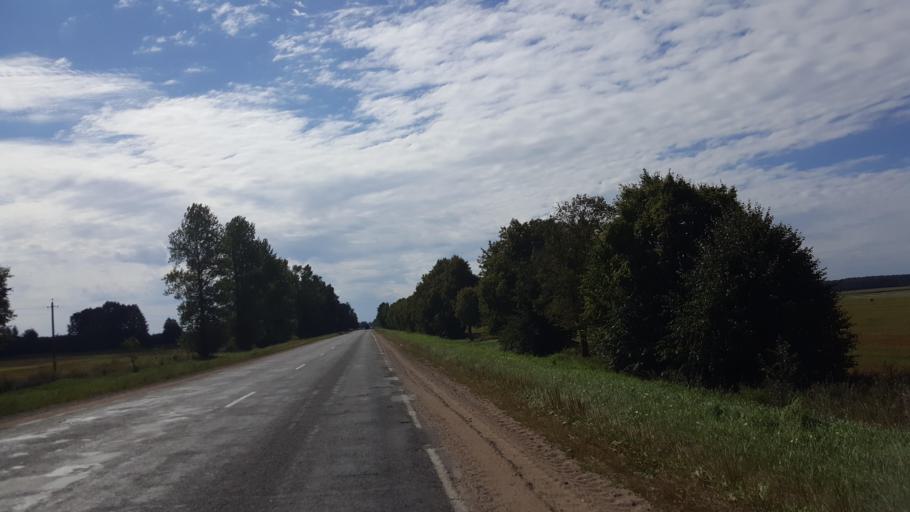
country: BY
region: Brest
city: Kamyanyets
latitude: 52.3610
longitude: 23.8914
